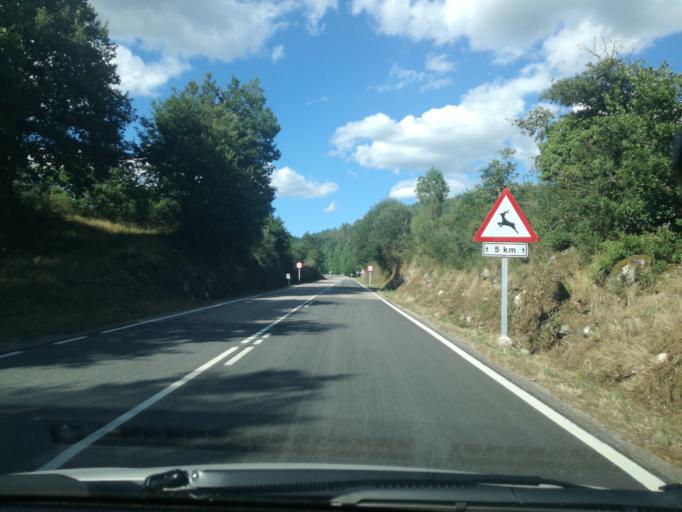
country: ES
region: Galicia
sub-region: Provincia de Ourense
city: Lobios
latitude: 41.8757
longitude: -8.0986
